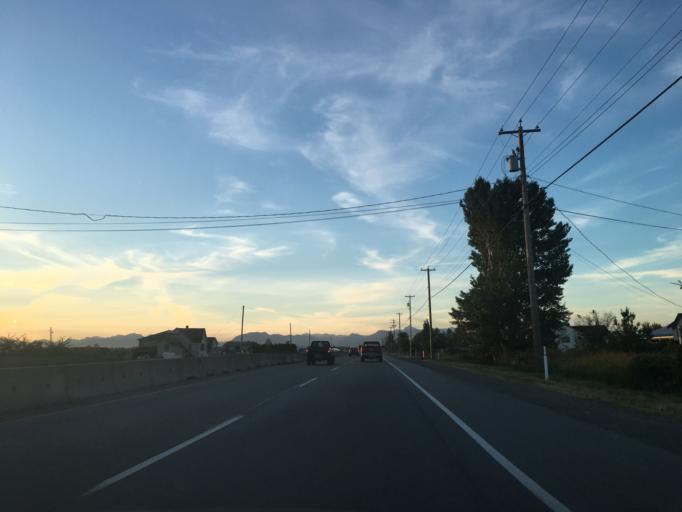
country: US
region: Washington
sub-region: Whatcom County
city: Blaine
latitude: 49.0682
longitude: -122.7355
